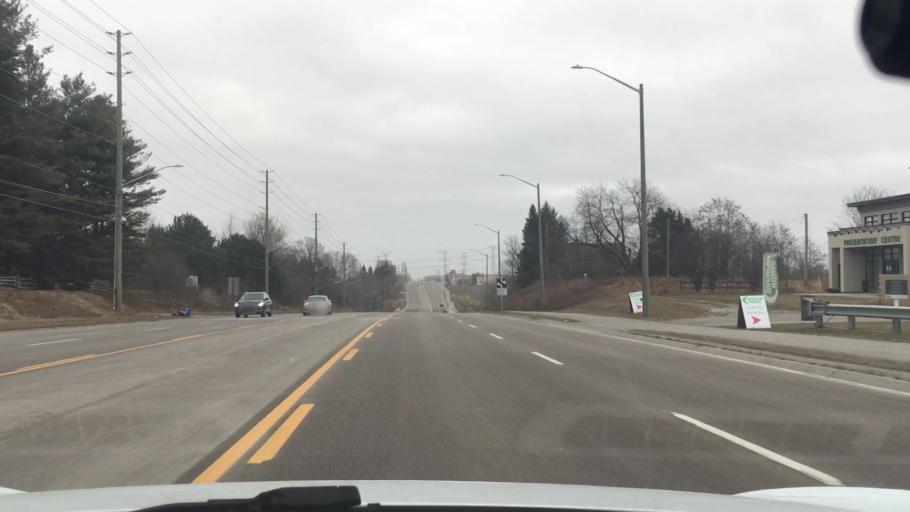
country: CA
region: Ontario
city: Ajax
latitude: 43.8903
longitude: -79.0637
